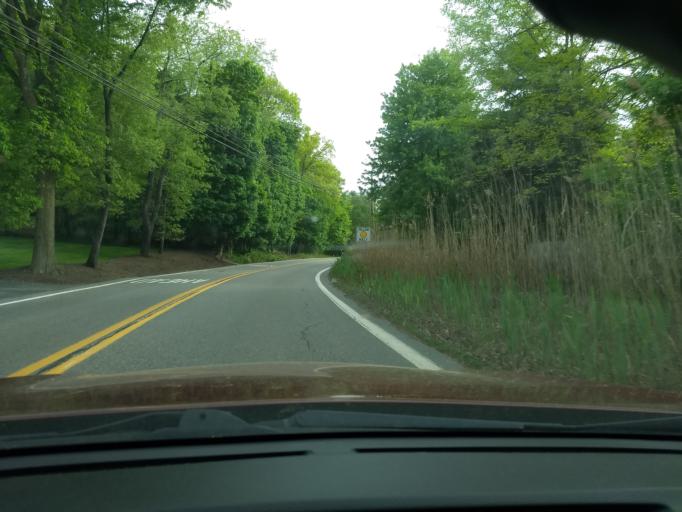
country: US
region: Pennsylvania
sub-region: Allegheny County
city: Allison Park
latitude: 40.5966
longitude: -79.9308
